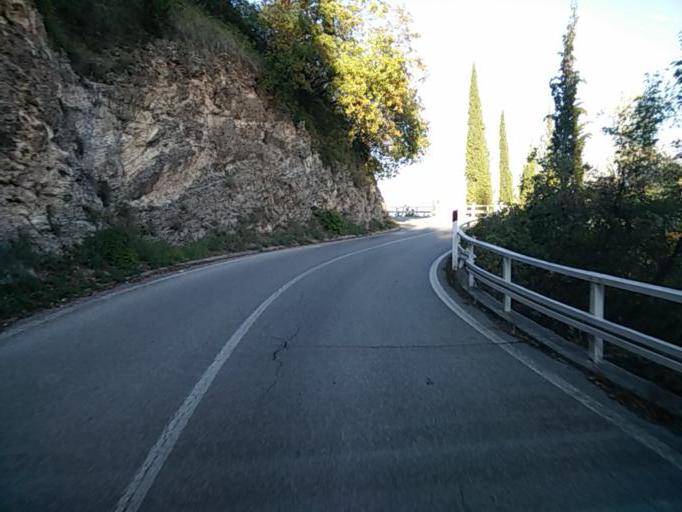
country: IT
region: Lombardy
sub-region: Provincia di Brescia
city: Gargnano
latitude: 45.6856
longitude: 10.6527
